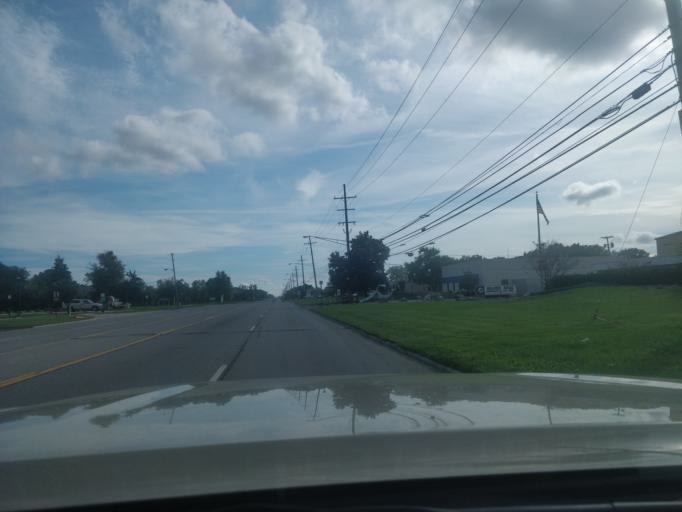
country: US
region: Michigan
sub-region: Wayne County
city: Woodhaven
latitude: 42.1666
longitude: -83.2271
